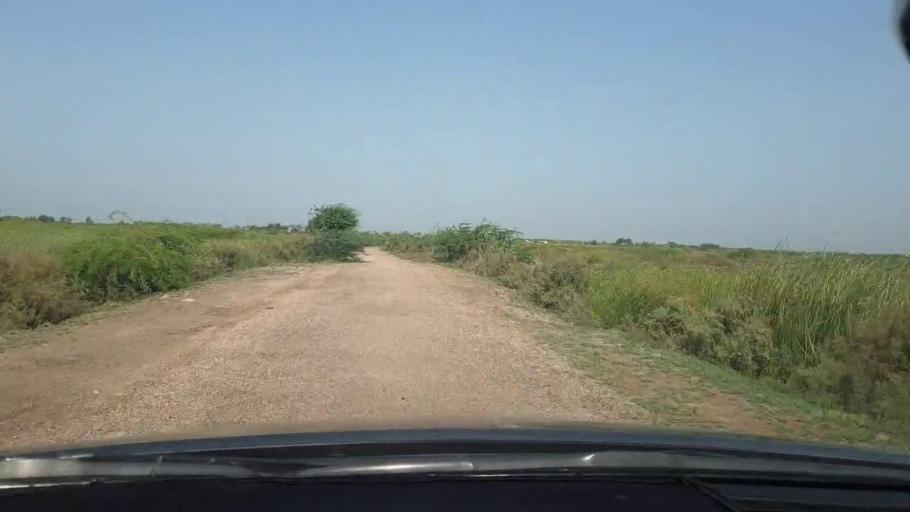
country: PK
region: Sindh
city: Tando Bago
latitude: 24.7106
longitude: 69.1078
